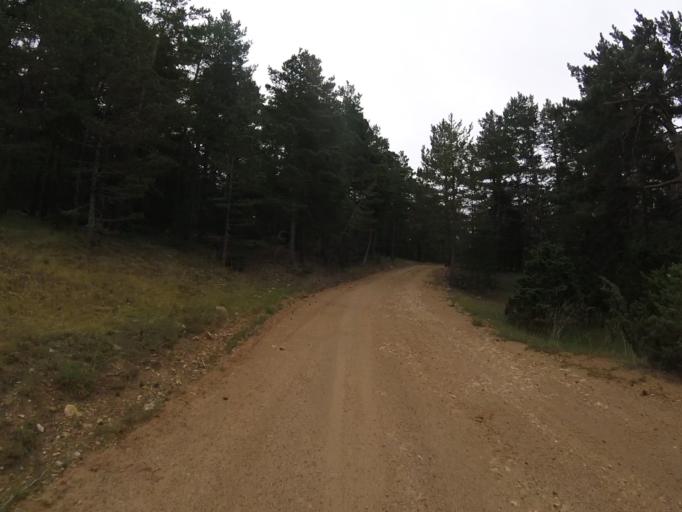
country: ES
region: Aragon
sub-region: Provincia de Teruel
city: Valdelinares
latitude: 40.3650
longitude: -0.6172
